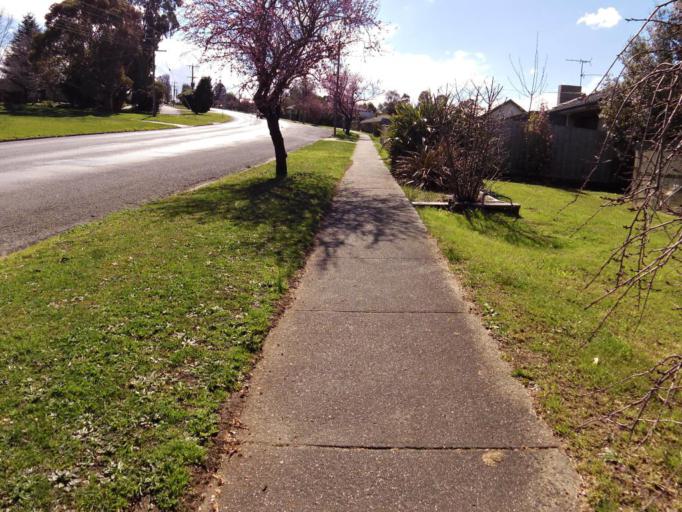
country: AU
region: Victoria
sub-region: Baw Baw
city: Warragul
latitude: -38.0209
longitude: 145.9547
